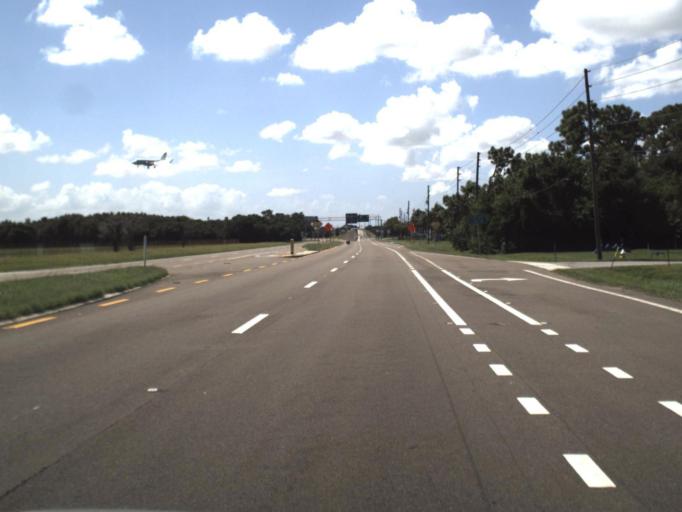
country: US
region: Florida
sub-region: Pinellas County
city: South Highpoint
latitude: 27.9007
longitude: -82.6931
